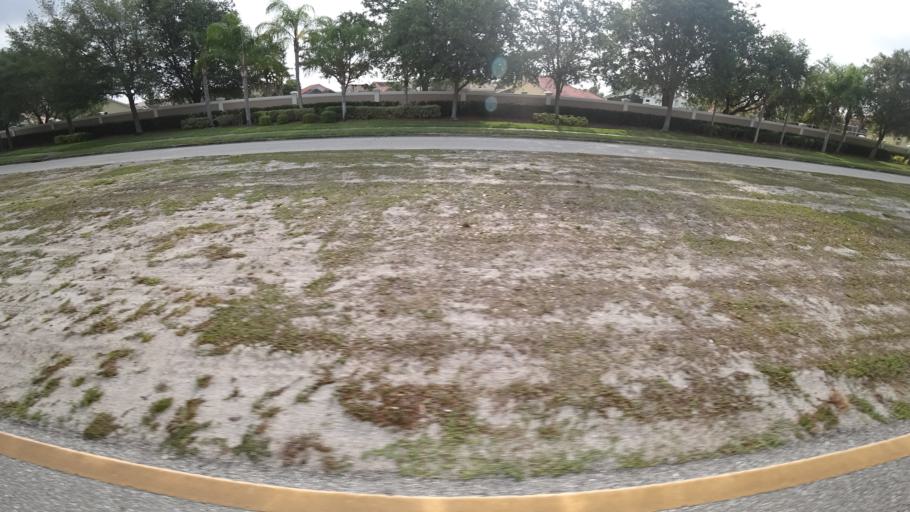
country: US
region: Florida
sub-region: Manatee County
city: Samoset
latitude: 27.4267
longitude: -82.5135
